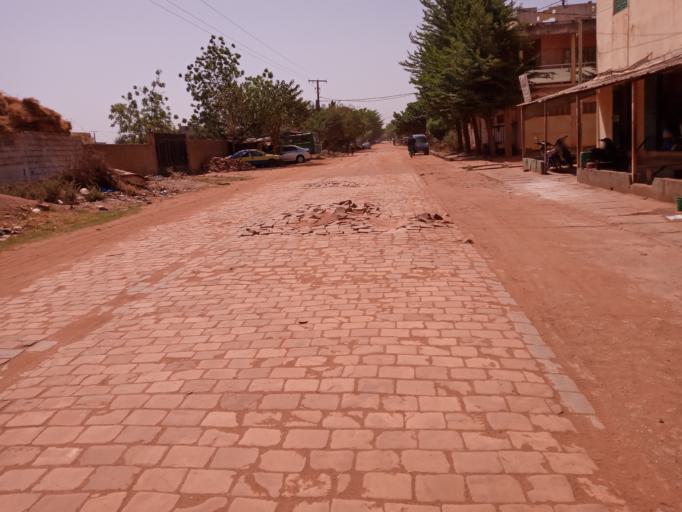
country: ML
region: Bamako
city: Bamako
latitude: 12.5864
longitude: -7.9563
